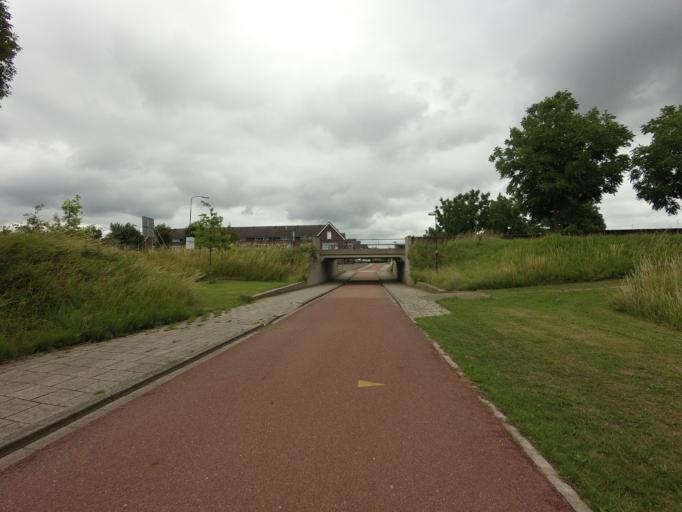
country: NL
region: Utrecht
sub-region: Gemeente Houten
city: Houten
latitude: 52.0112
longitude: 5.1845
